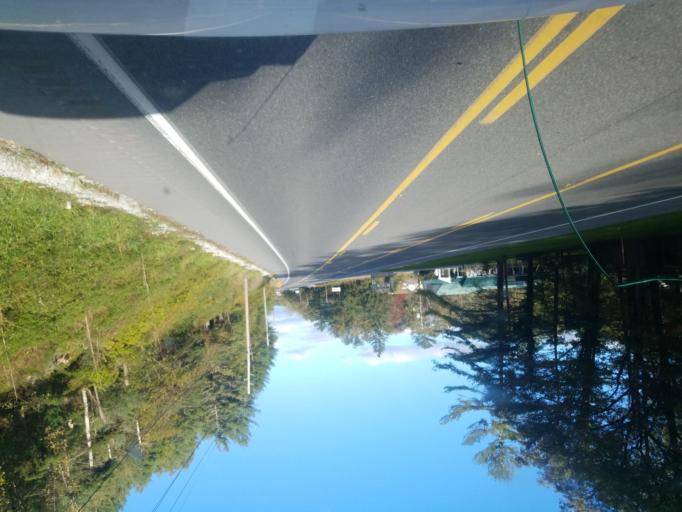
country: US
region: Pennsylvania
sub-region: Franklin County
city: Fayetteville
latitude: 39.9015
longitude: -77.4593
